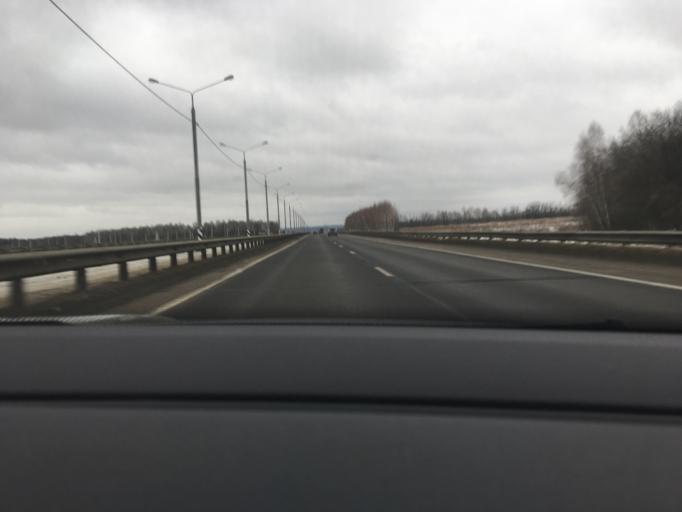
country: RU
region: Tula
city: Zaokskiy
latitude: 54.8000
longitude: 37.4849
